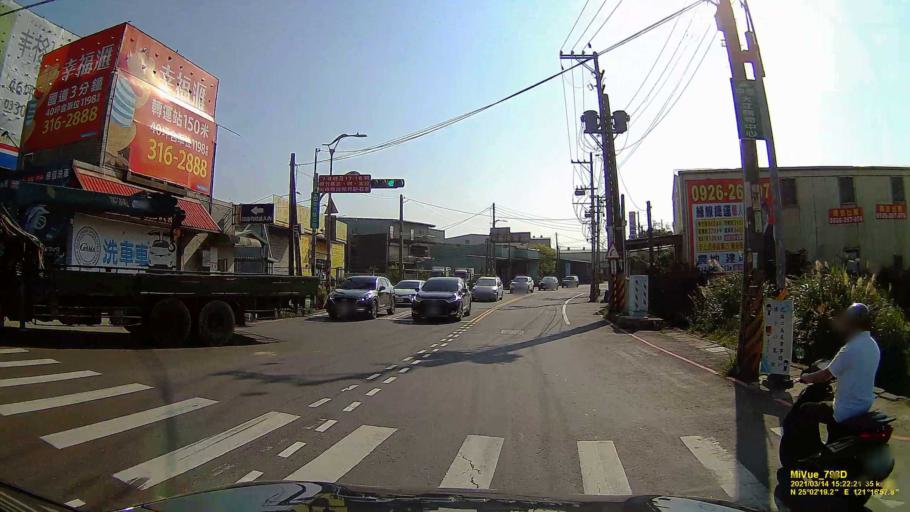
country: TW
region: Taiwan
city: Taoyuan City
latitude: 25.0385
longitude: 121.2826
